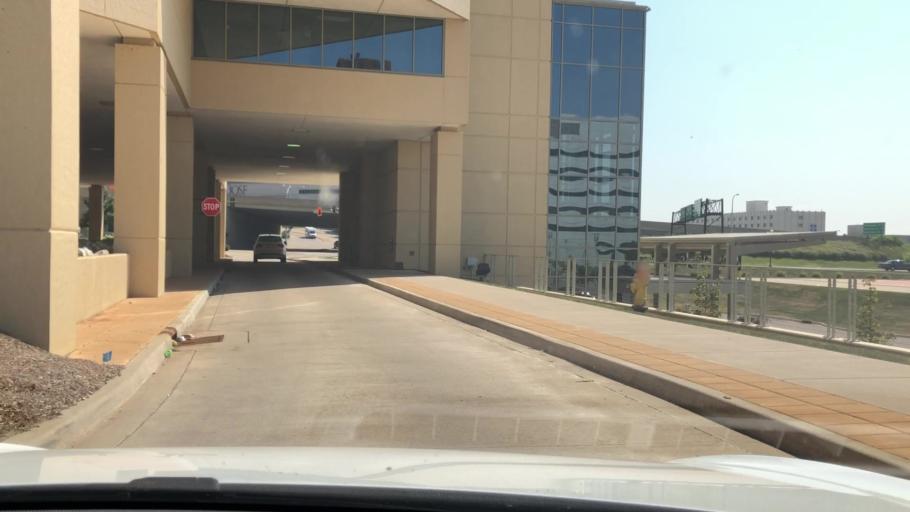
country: US
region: Illinois
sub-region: Peoria County
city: Peoria
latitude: 40.6996
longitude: -89.5952
